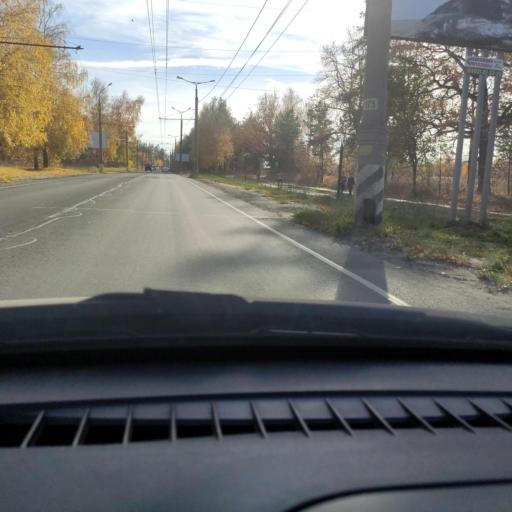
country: RU
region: Samara
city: Tol'yatti
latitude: 53.4941
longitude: 49.3864
